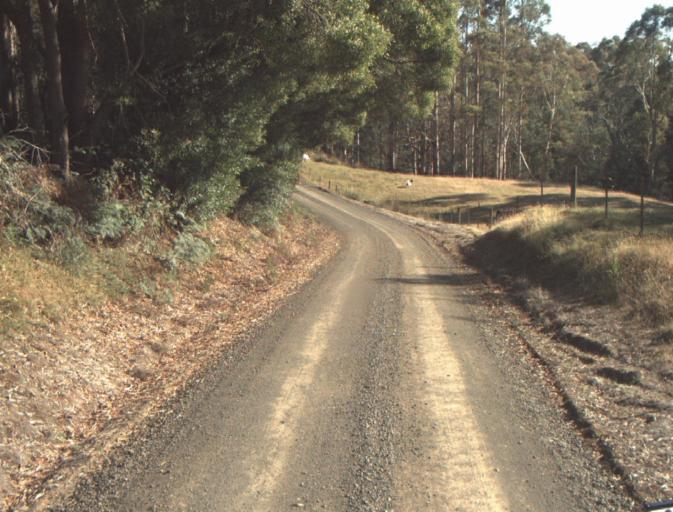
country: AU
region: Tasmania
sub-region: Launceston
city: Mayfield
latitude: -41.2987
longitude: 147.1977
